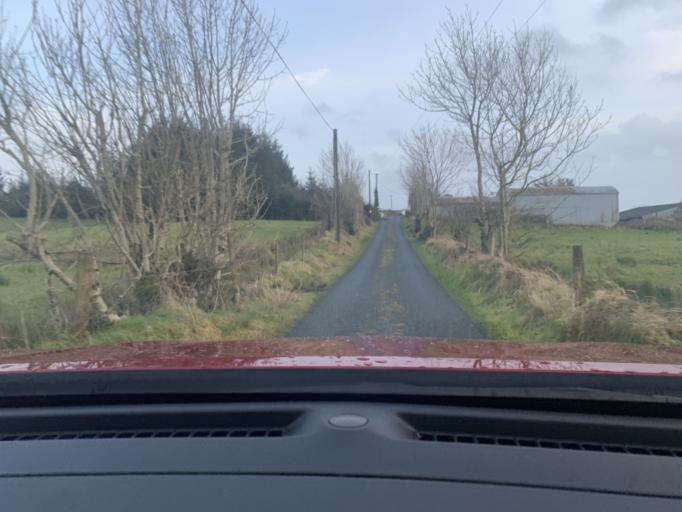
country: IE
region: Connaught
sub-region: Roscommon
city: Ballaghaderreen
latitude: 53.9501
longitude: -8.5163
